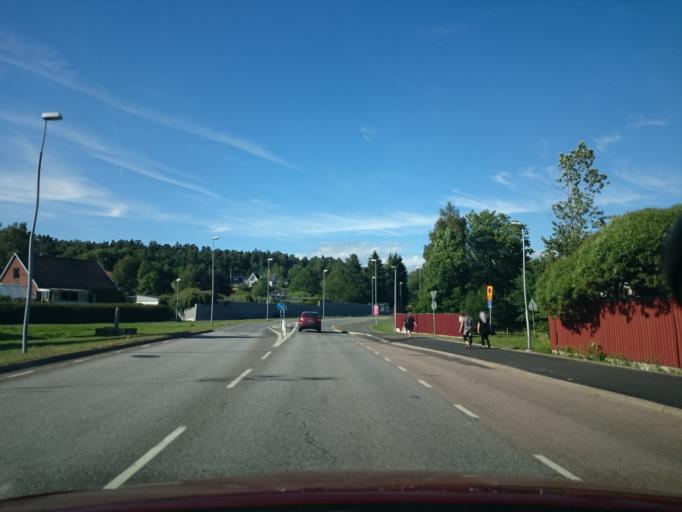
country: SE
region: Vaestra Goetaland
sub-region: Lerums Kommun
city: Lerum
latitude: 57.7762
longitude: 12.2770
